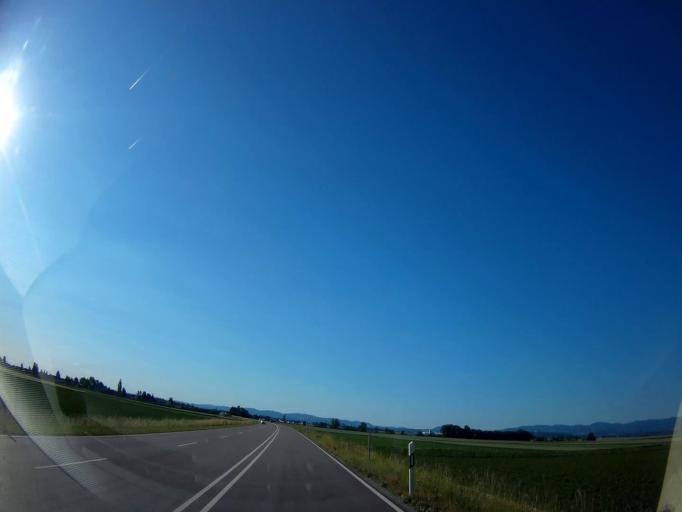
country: DE
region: Bavaria
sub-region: Lower Bavaria
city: Oberschneiding
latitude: 48.8123
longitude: 12.6527
